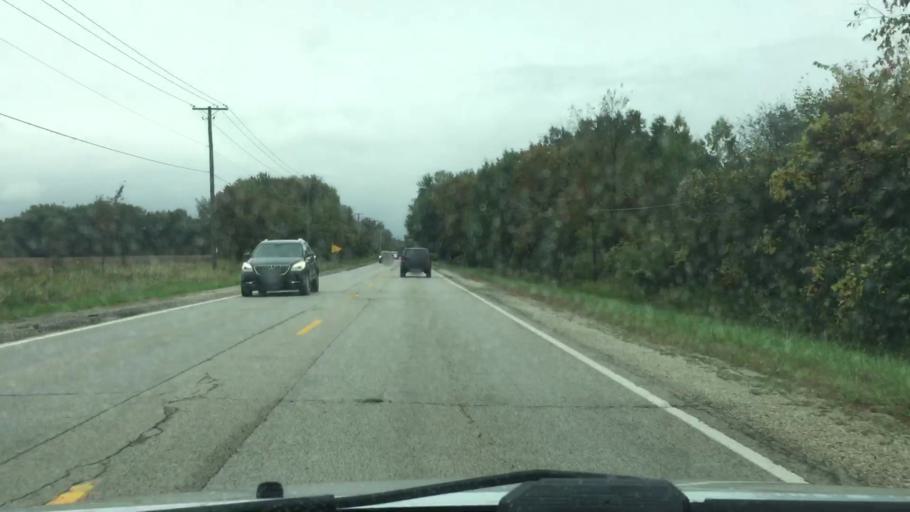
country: US
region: Illinois
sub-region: McHenry County
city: Richmond
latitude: 42.4642
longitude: -88.3066
